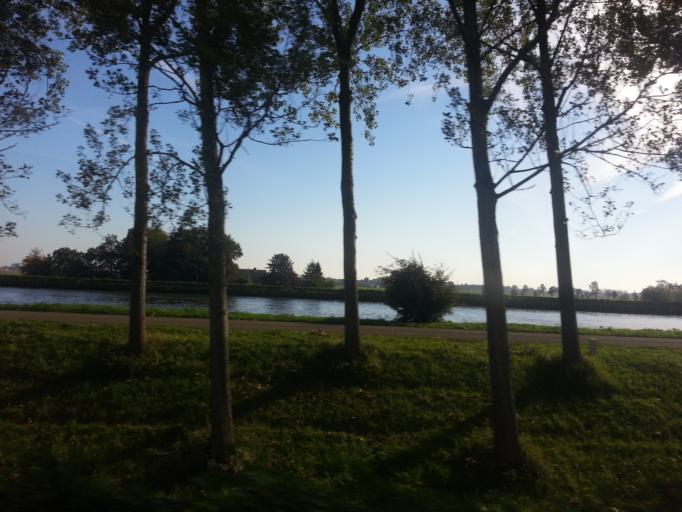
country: NL
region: Utrecht
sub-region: Stichtse Vecht
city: Vreeland
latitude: 52.2332
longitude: 5.0074
